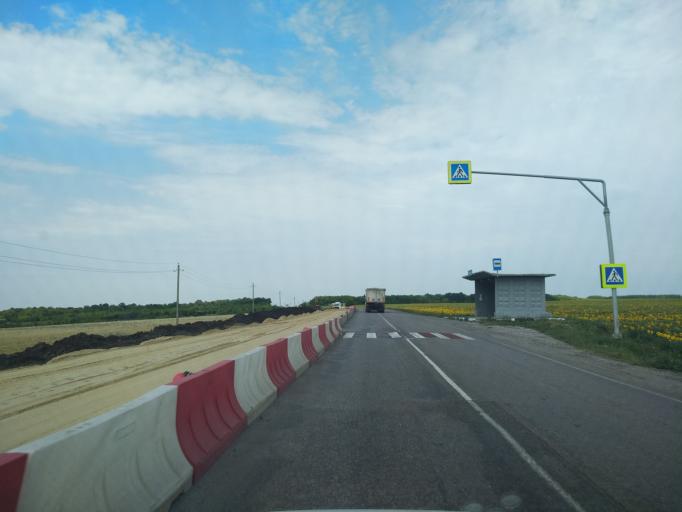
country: RU
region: Voronezj
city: Verkhnyaya Khava
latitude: 51.6776
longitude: 39.8022
